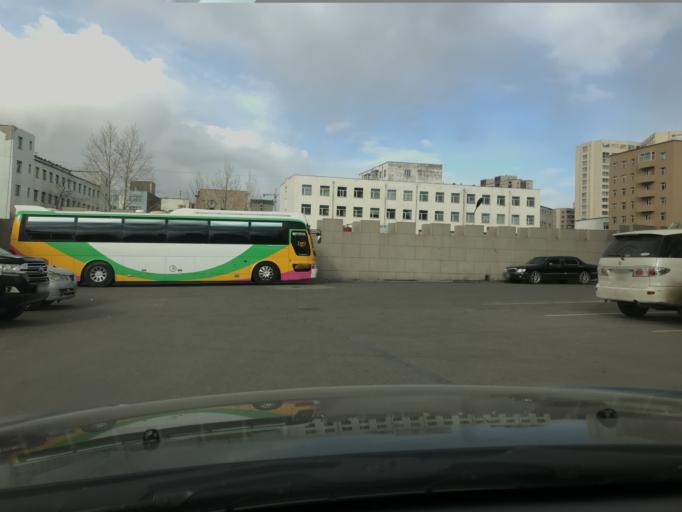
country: MN
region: Ulaanbaatar
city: Ulaanbaatar
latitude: 47.9129
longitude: 106.9723
